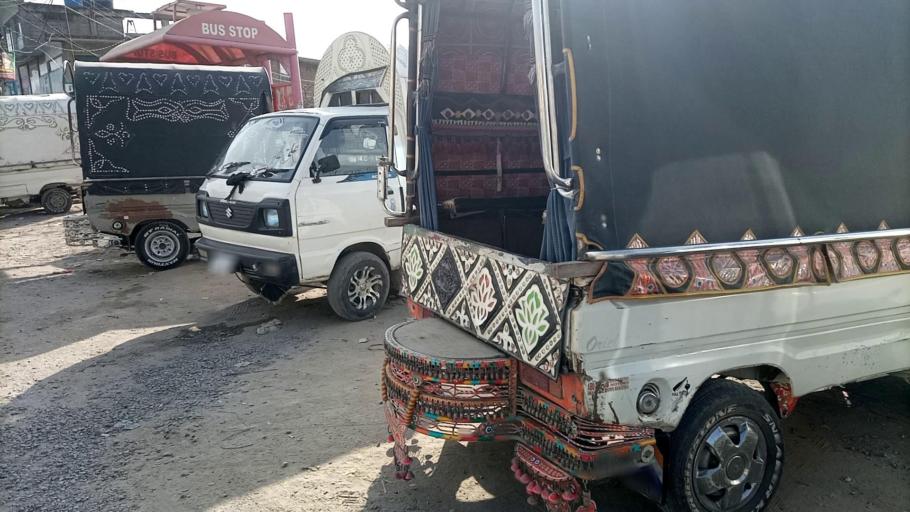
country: PK
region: Khyber Pakhtunkhwa
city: Abbottabad
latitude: 34.2192
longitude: 73.2446
